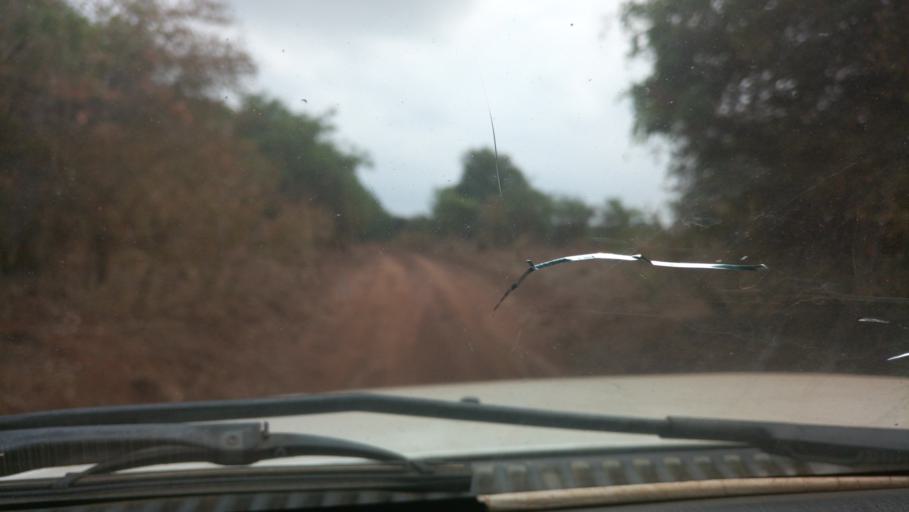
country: KE
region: Nairobi Area
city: Nairobi
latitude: -1.3551
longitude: 36.7764
